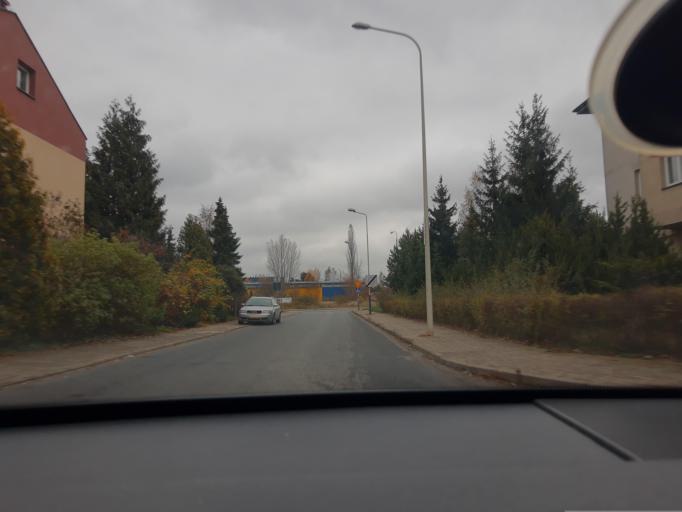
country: PL
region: Lodz Voivodeship
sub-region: Powiat pabianicki
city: Konstantynow Lodzki
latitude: 51.7358
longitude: 19.3761
